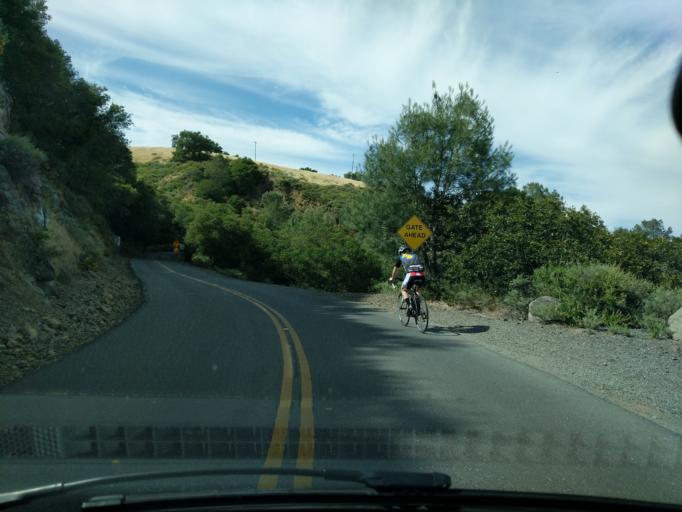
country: US
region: California
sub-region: Contra Costa County
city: Blackhawk
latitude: 37.8414
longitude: -121.9214
